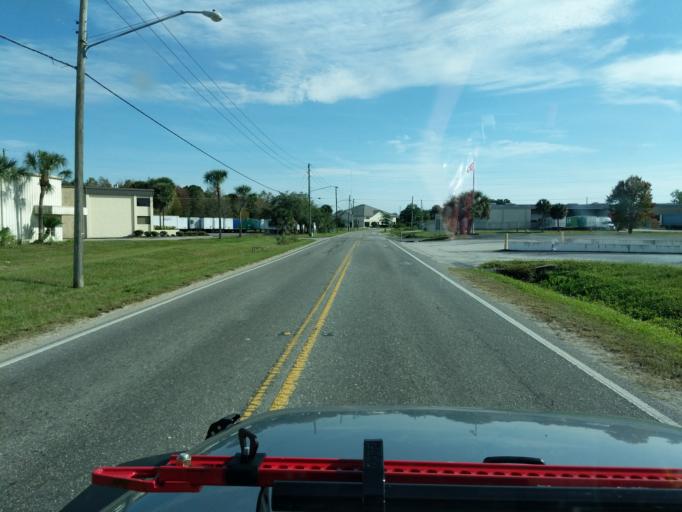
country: US
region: Florida
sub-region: Orange County
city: Ocoee
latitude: 28.5636
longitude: -81.5482
